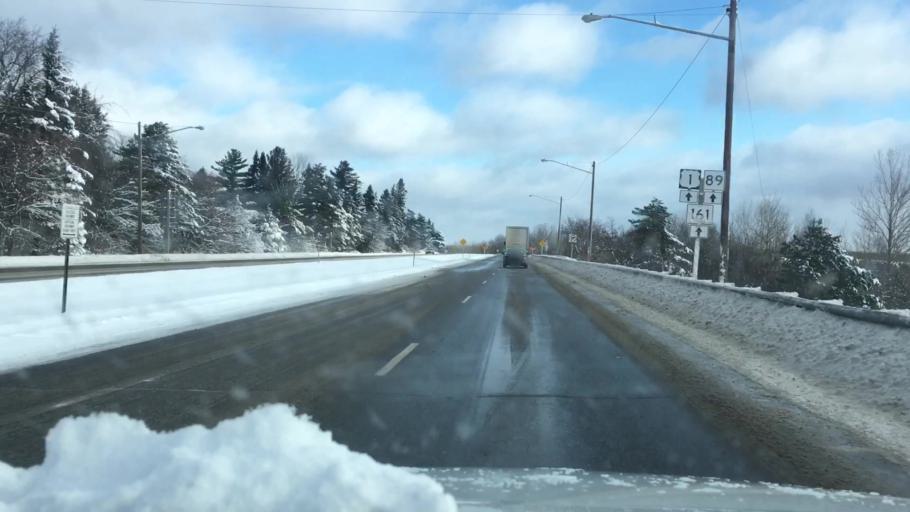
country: US
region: Maine
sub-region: Aroostook County
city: Caribou
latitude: 46.8617
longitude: -68.0023
